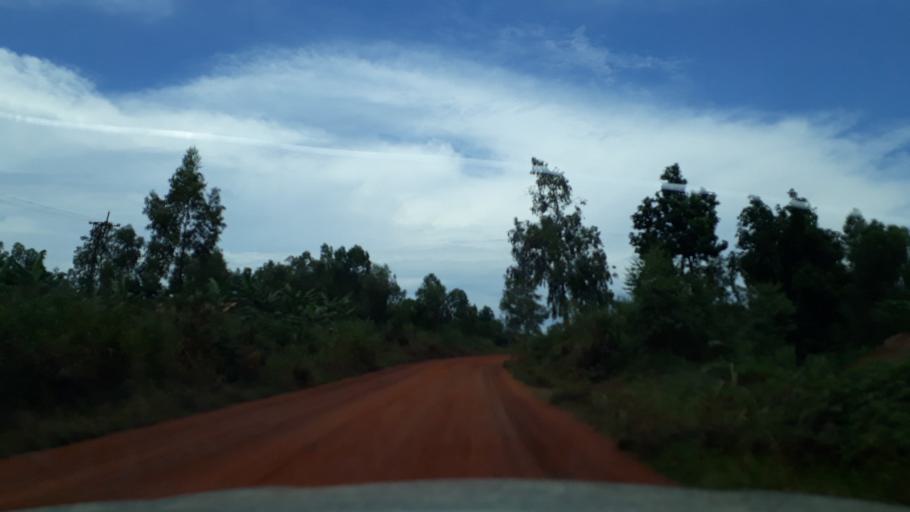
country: CD
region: Eastern Province
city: Bunia
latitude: 1.6951
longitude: 30.2801
